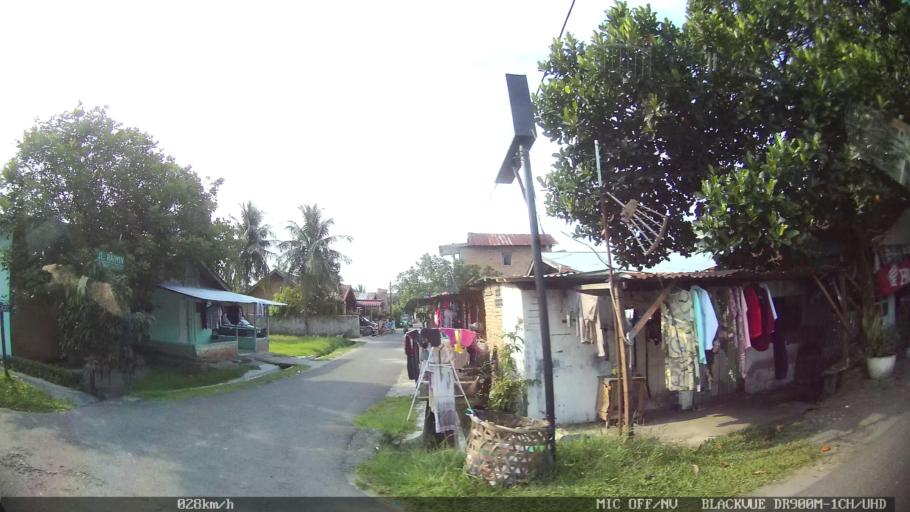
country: ID
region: North Sumatra
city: Binjai
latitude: 3.6047
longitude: 98.4968
